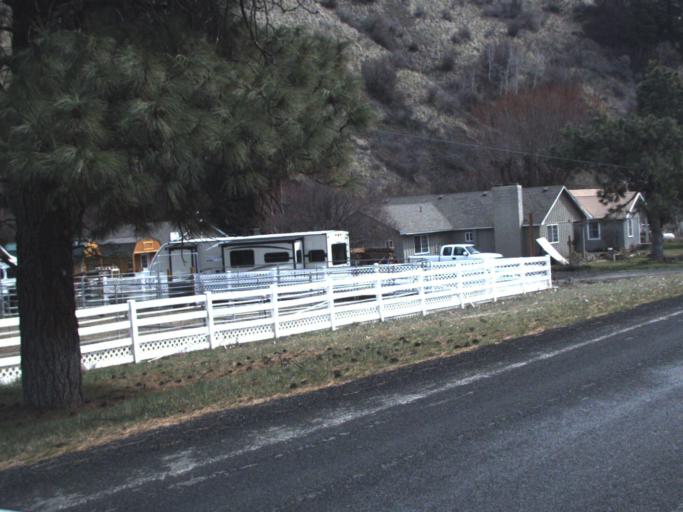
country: US
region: Washington
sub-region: Yakima County
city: Tieton
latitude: 46.8368
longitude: -120.9417
